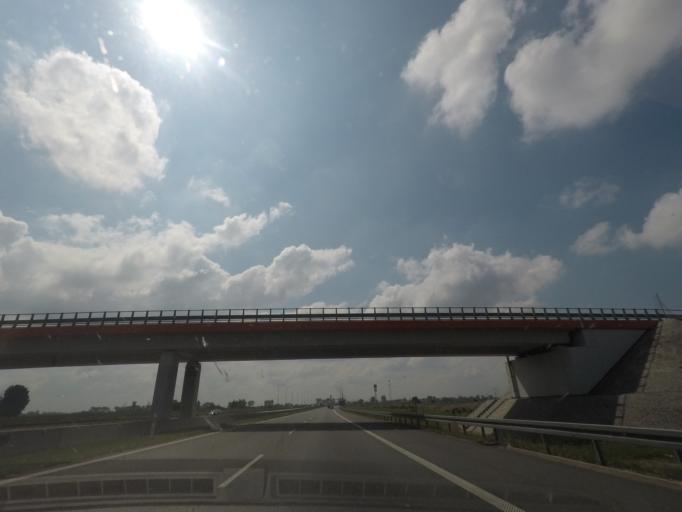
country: PL
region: Lodz Voivodeship
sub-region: Powiat kutnowski
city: Krzyzanow
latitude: 52.1923
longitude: 19.4874
